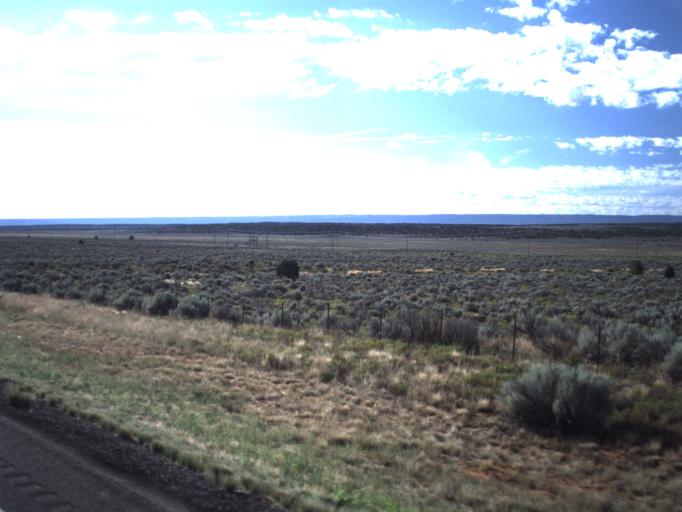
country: US
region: Utah
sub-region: Kane County
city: Kanab
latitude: 37.0260
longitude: -112.4674
